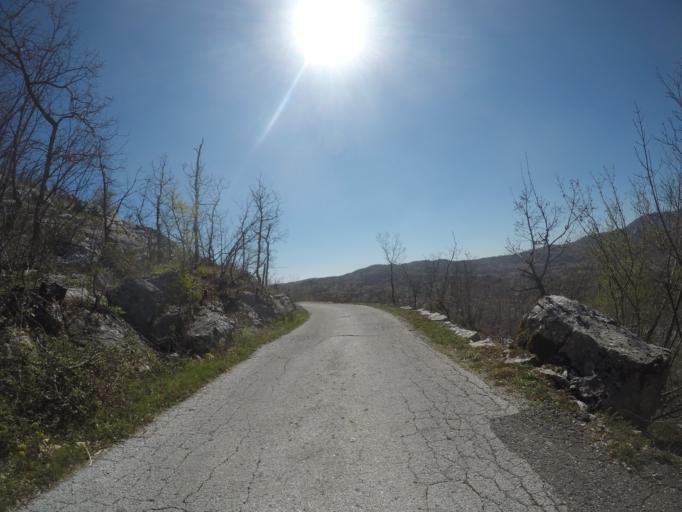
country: ME
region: Cetinje
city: Cetinje
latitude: 42.5283
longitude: 18.9603
